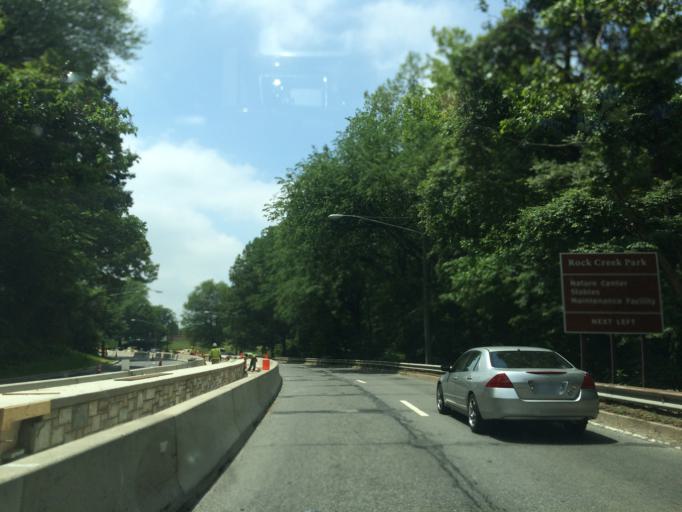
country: US
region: Maryland
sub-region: Montgomery County
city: Chevy Chase
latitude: 38.9619
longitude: -77.0507
